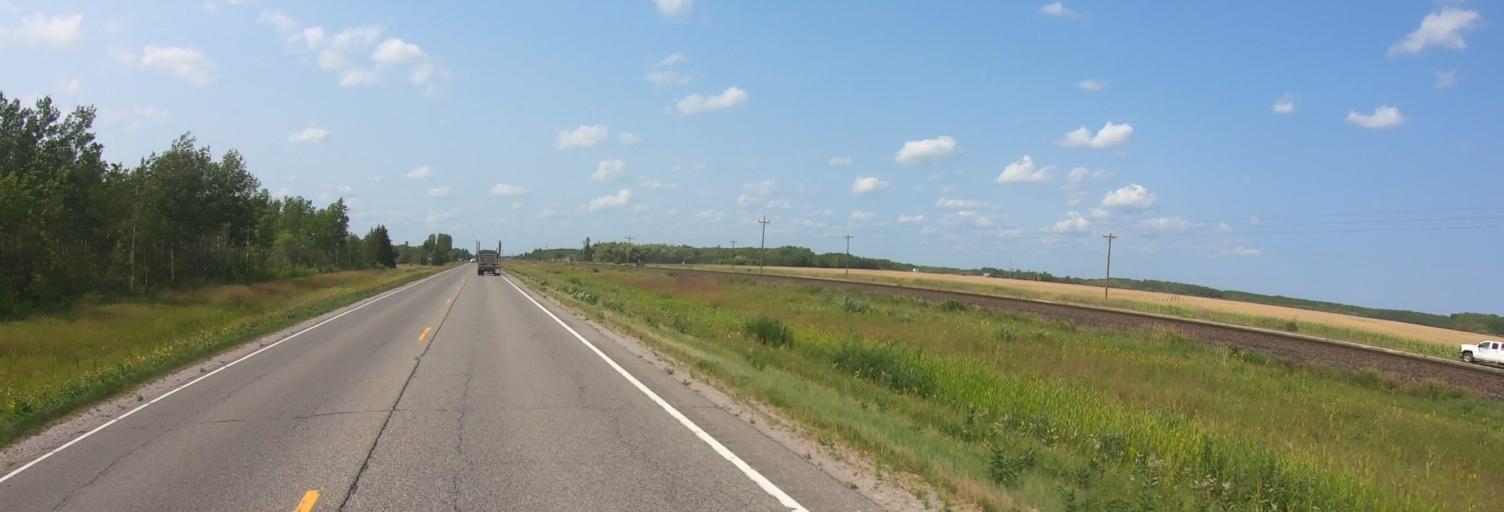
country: US
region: Minnesota
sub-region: Roseau County
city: Warroad
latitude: 48.8825
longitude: -95.2903
